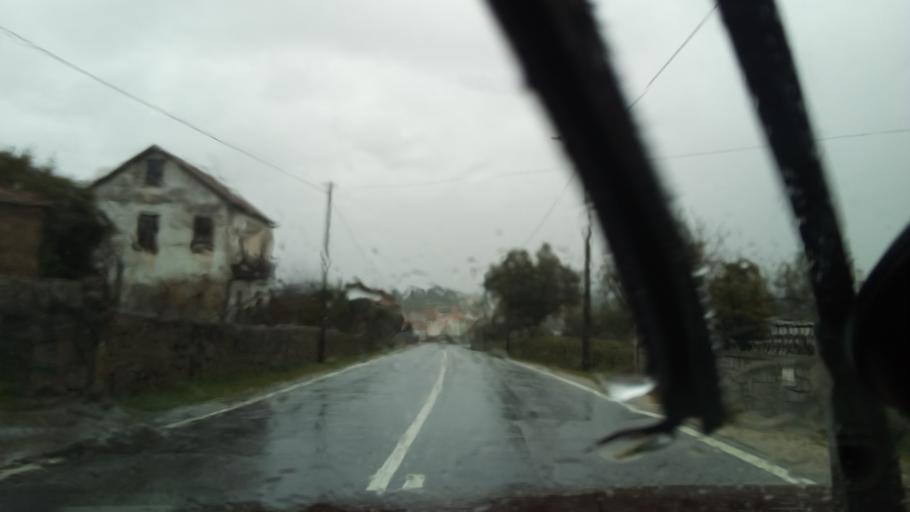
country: PT
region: Guarda
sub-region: Fornos de Algodres
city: Fornos de Algodres
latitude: 40.5479
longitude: -7.5312
